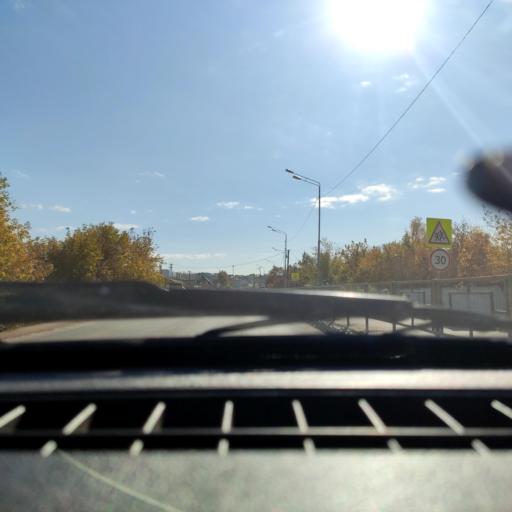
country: RU
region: Bashkortostan
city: Ufa
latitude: 54.6118
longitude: 55.9387
